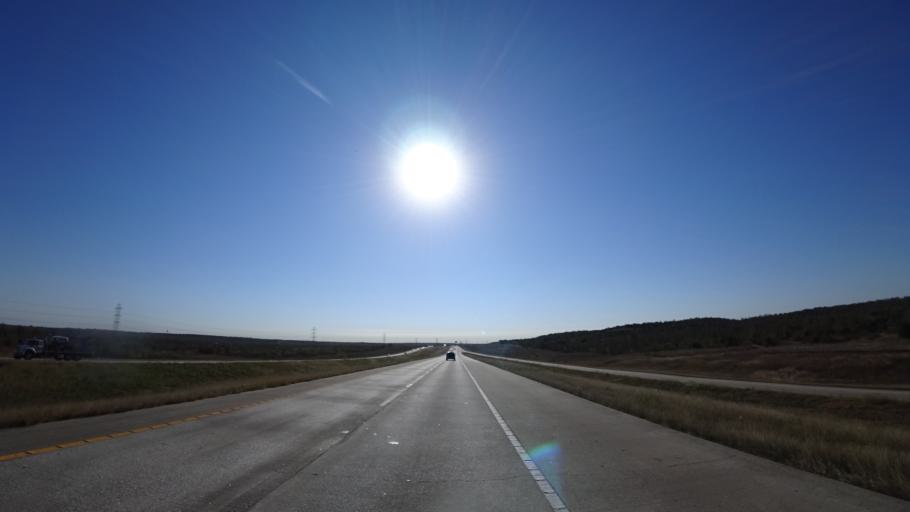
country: US
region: Texas
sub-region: Travis County
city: Manor
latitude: 30.3215
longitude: -97.5790
